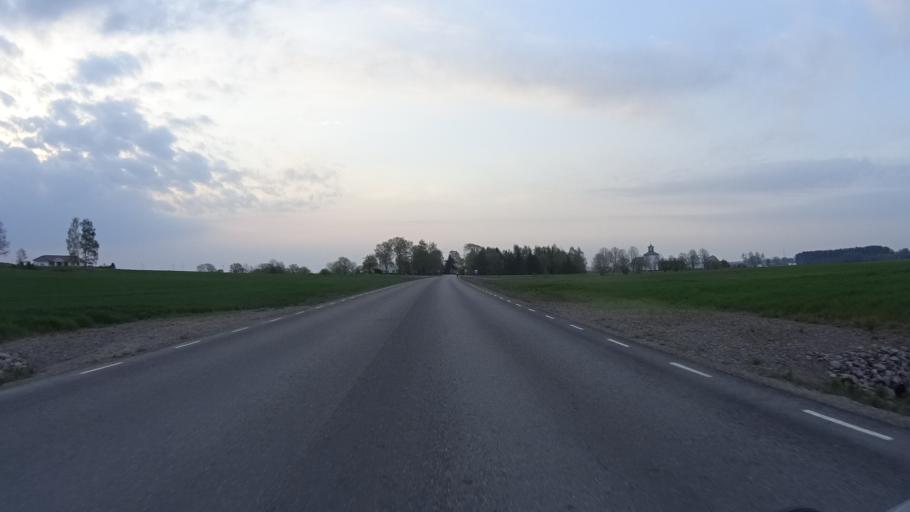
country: SE
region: Vaestra Goetaland
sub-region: Gotene Kommun
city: Kallby
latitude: 58.4970
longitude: 13.3103
